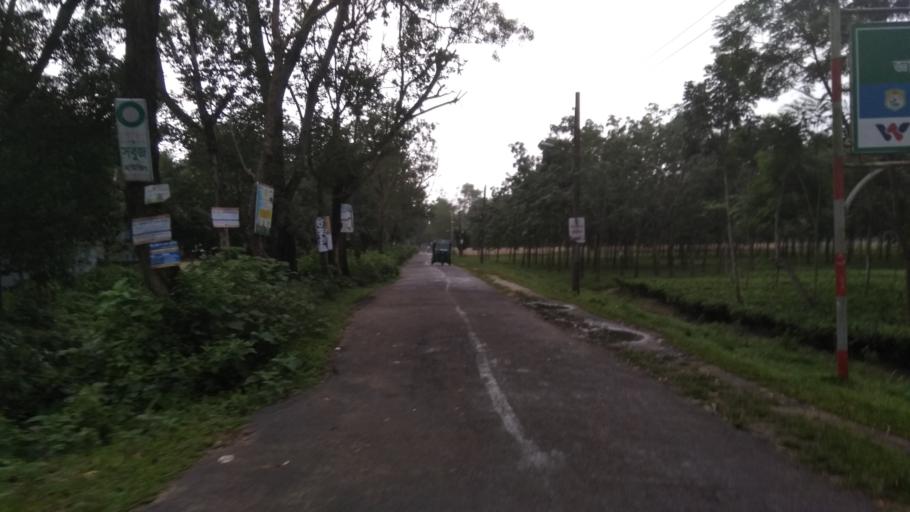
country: IN
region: Tripura
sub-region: Dhalai
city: Kamalpur
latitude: 24.3013
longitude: 91.7352
